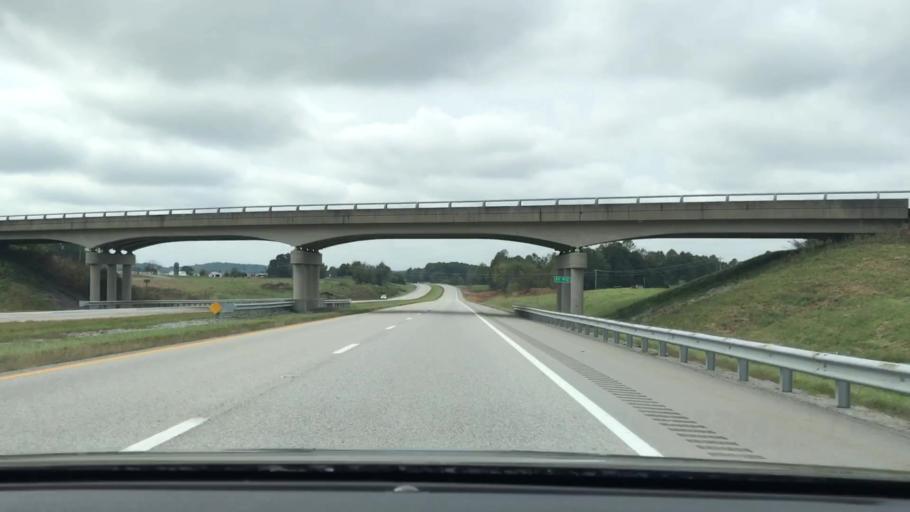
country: US
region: Kentucky
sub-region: Russell County
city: Russell Springs
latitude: 37.0854
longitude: -84.9301
